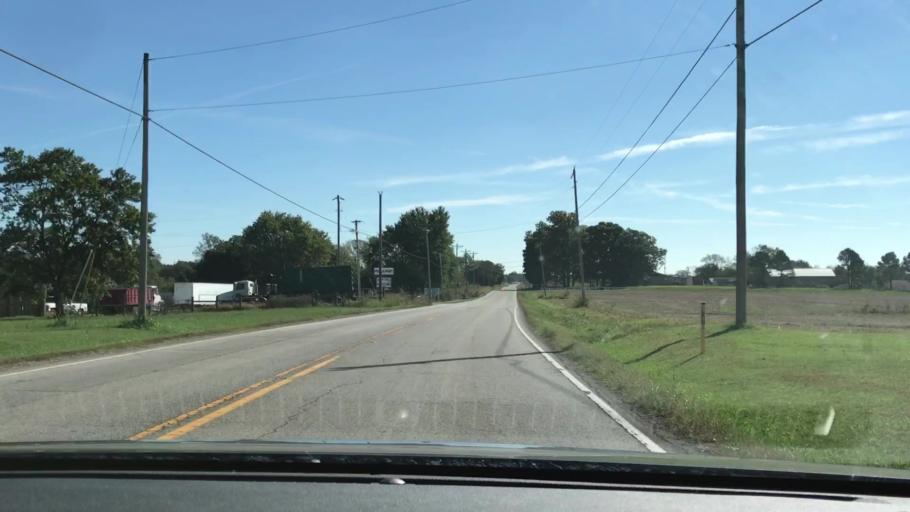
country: US
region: Kentucky
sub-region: Christian County
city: Hopkinsville
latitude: 36.8626
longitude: -87.4431
